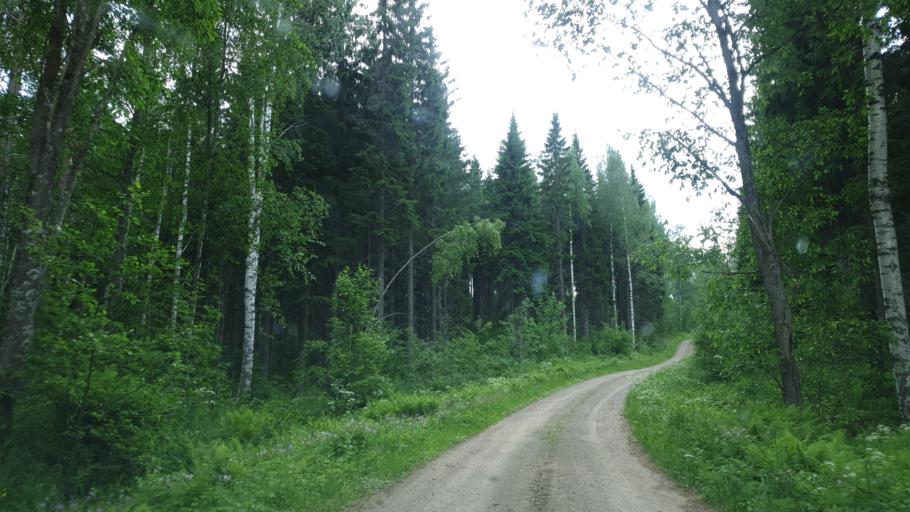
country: FI
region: Northern Savo
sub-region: Koillis-Savo
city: Kaavi
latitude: 62.9777
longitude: 28.7560
